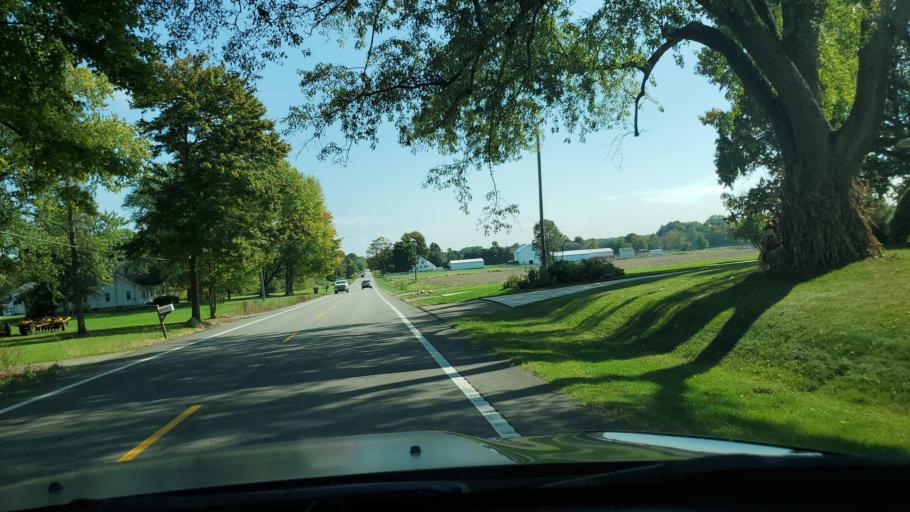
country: US
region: Ohio
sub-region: Trumbull County
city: Cortland
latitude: 41.3887
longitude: -80.6460
